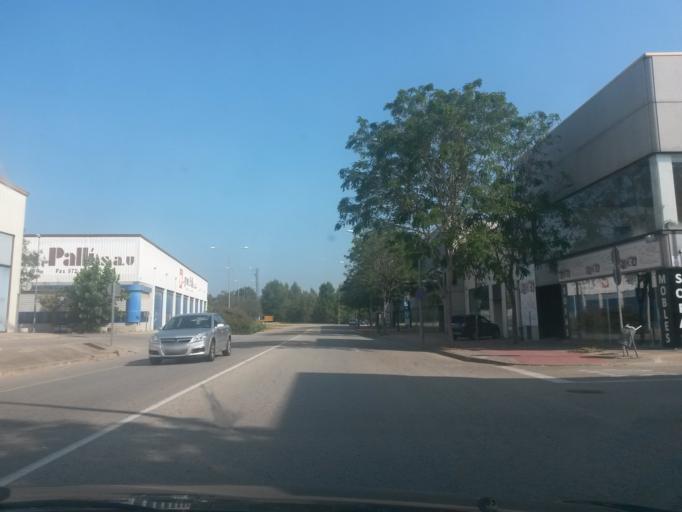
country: ES
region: Catalonia
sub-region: Provincia de Girona
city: Fornells de la Selva
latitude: 41.9541
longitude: 2.8080
